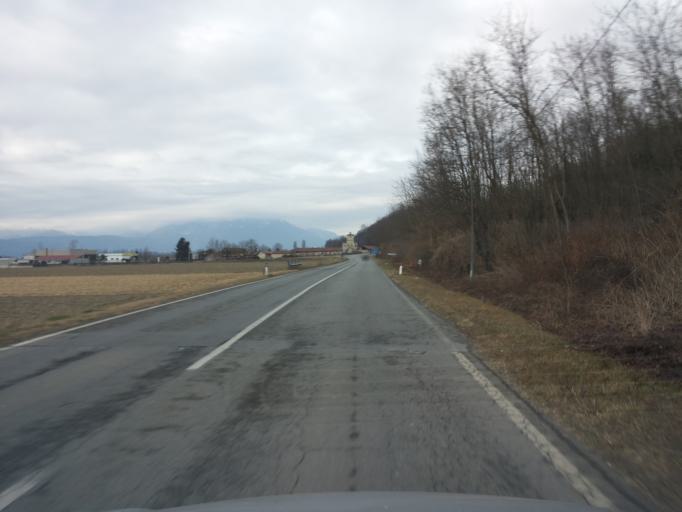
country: IT
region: Piedmont
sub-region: Provincia di Torino
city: Vestigne
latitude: 45.3948
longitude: 7.9447
